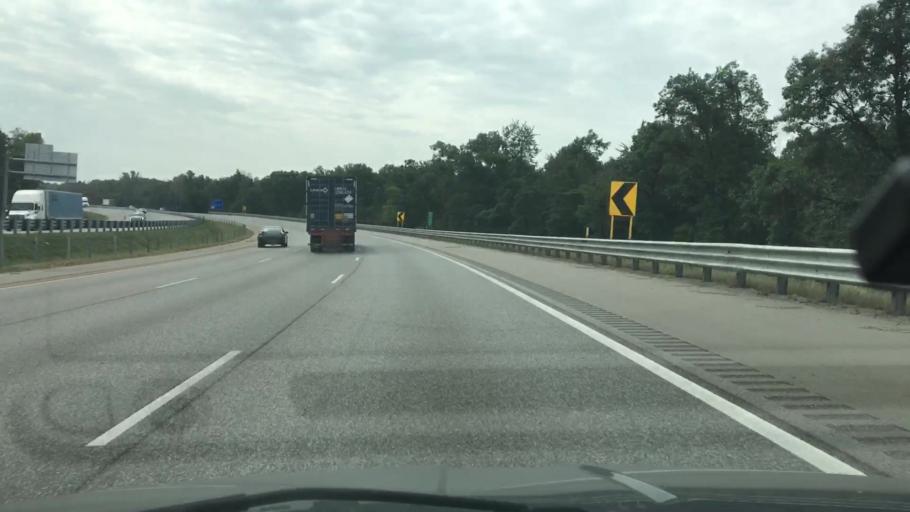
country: US
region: Michigan
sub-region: Berrien County
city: Stevensville
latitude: 42.0214
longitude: -86.5322
